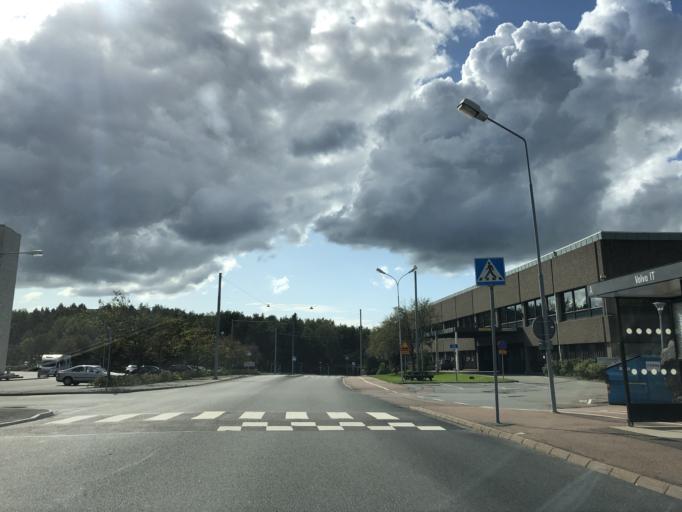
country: SE
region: Vaestra Goetaland
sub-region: Goteborg
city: Majorna
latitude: 57.7255
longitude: 11.8570
